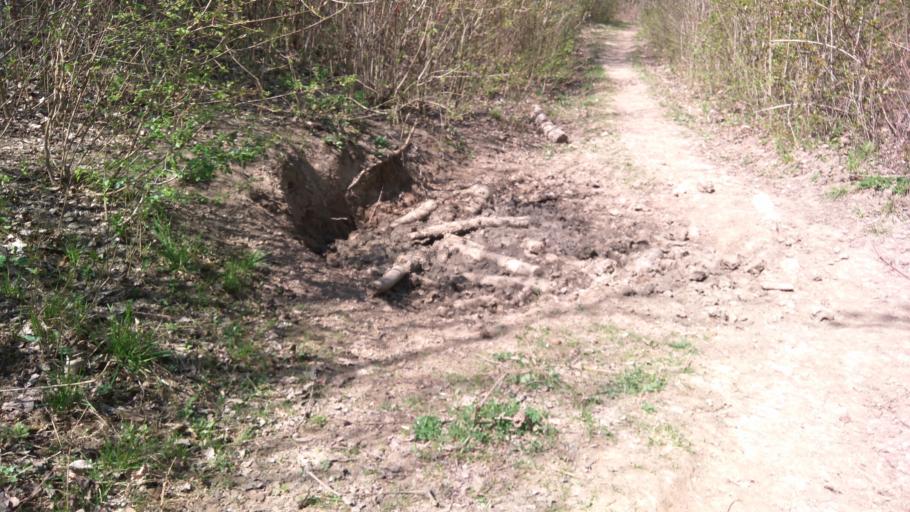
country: HU
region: Pest
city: Pilisborosjeno
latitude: 47.6261
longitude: 18.9965
